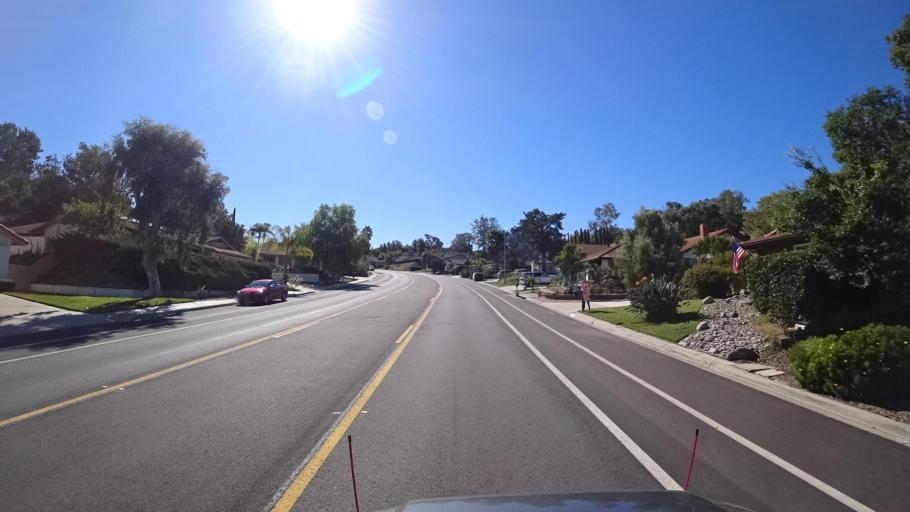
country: US
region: California
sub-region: San Diego County
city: Bonita
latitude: 32.6632
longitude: -117.0011
